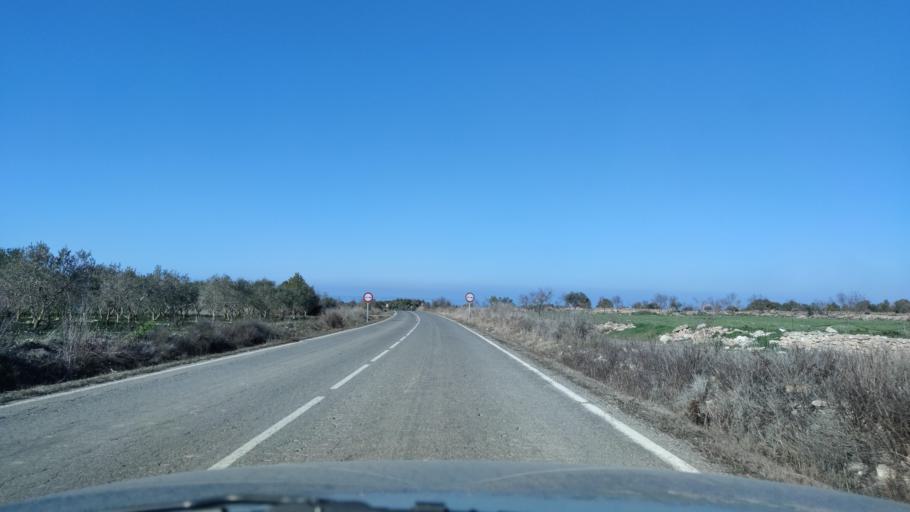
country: ES
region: Catalonia
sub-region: Provincia de Lleida
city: Maials
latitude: 41.3229
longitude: 0.4233
